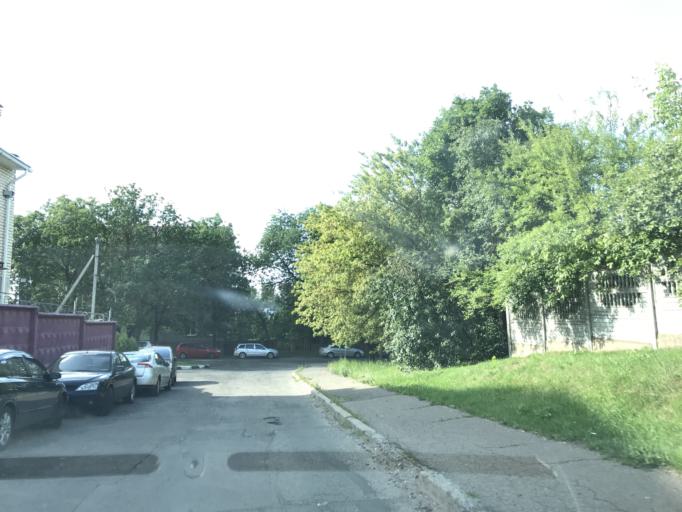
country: BY
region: Minsk
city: Bal'shavik
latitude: 53.9525
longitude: 27.5957
